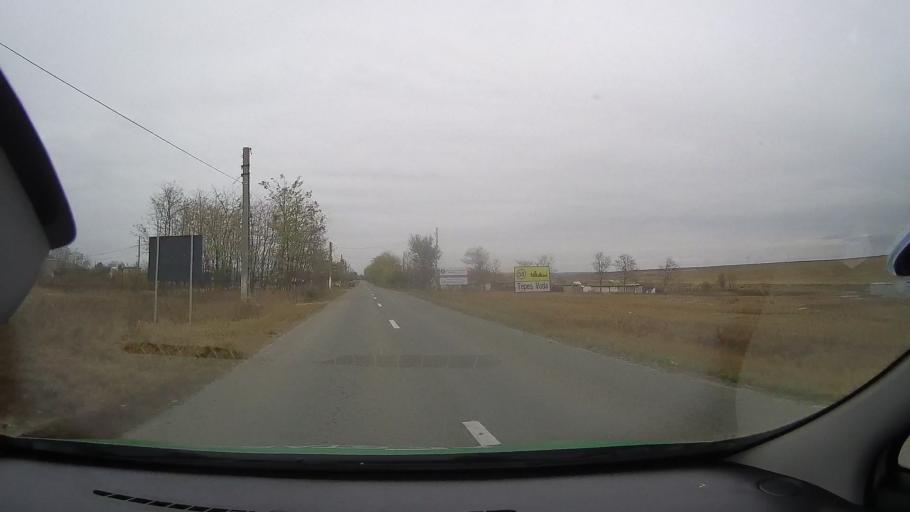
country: RO
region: Constanta
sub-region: Comuna Silistea
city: Silistea
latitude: 44.4401
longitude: 28.2301
